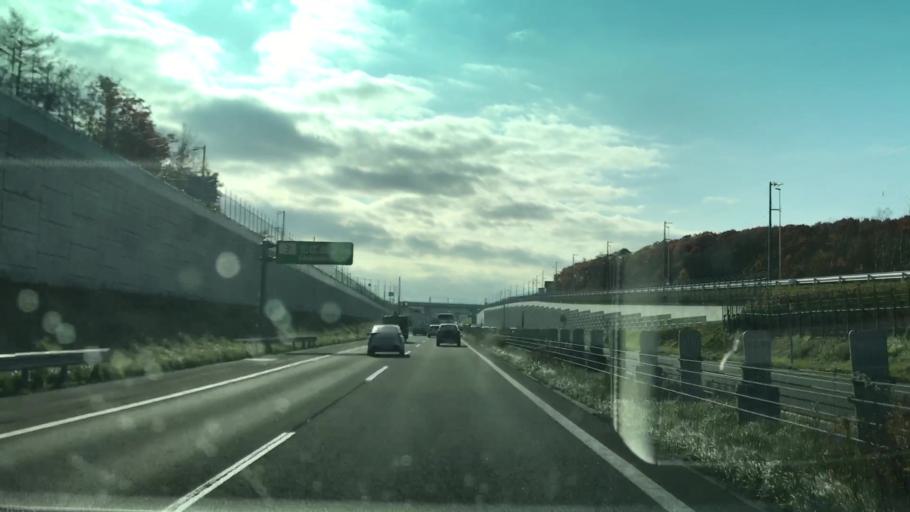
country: JP
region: Hokkaido
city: Kitahiroshima
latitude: 42.9983
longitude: 141.4684
